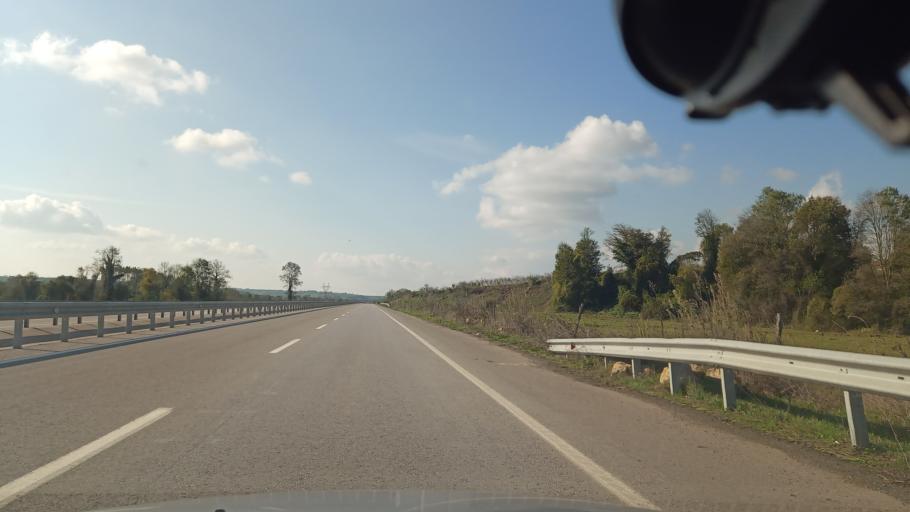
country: TR
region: Sakarya
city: Kaynarca
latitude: 41.0843
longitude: 30.4190
